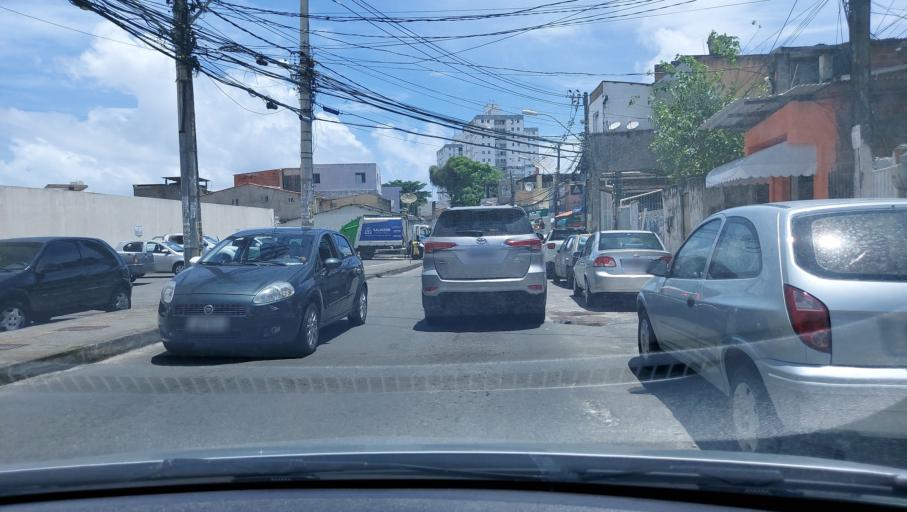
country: BR
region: Bahia
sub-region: Salvador
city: Salvador
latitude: -12.9858
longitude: -38.4763
